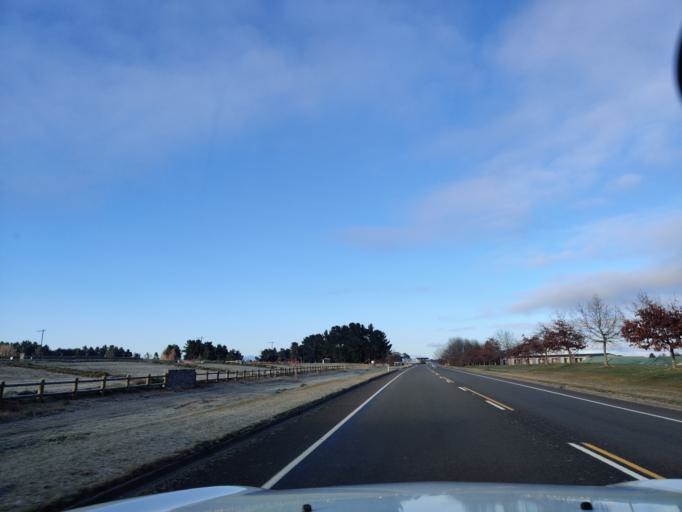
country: NZ
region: Waikato
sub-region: Taupo District
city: Taupo
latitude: -38.7301
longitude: 176.0739
